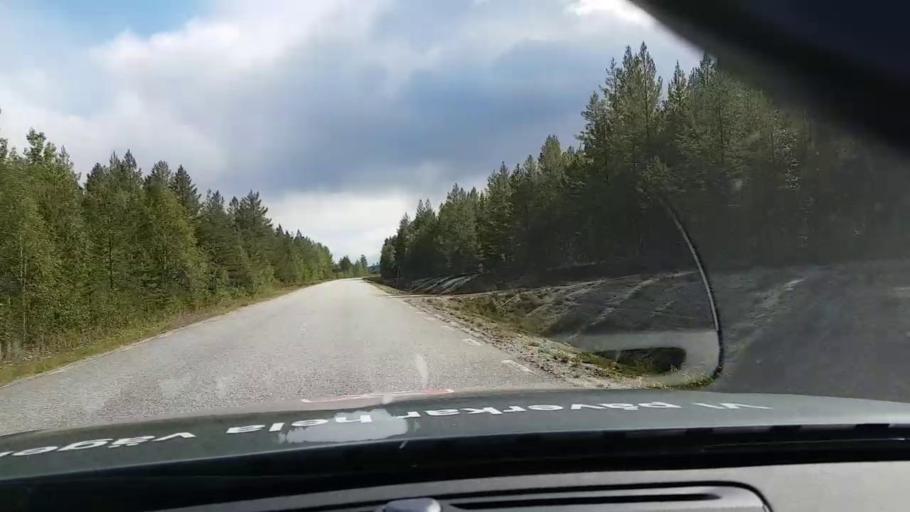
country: SE
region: Vaesterbotten
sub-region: Asele Kommun
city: Asele
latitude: 63.9092
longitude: 17.3394
